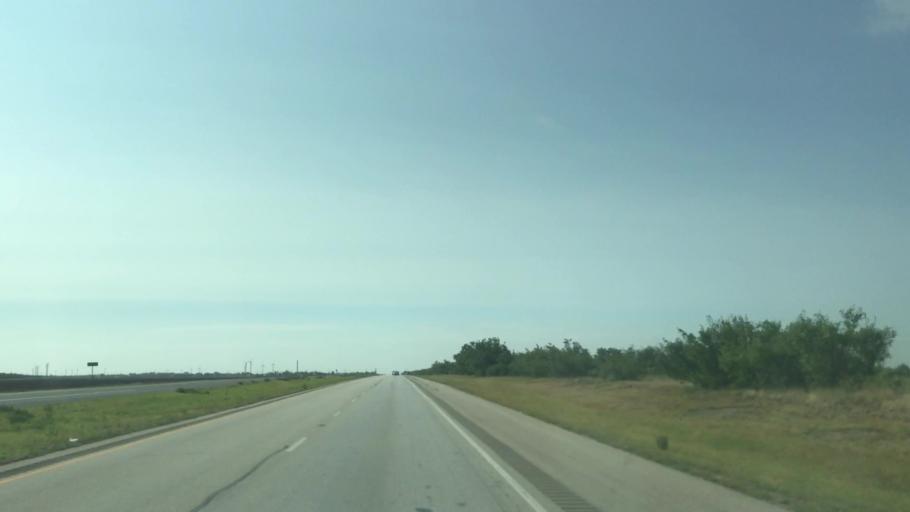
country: US
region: Texas
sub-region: Scurry County
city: Snyder
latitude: 32.6527
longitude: -100.7777
